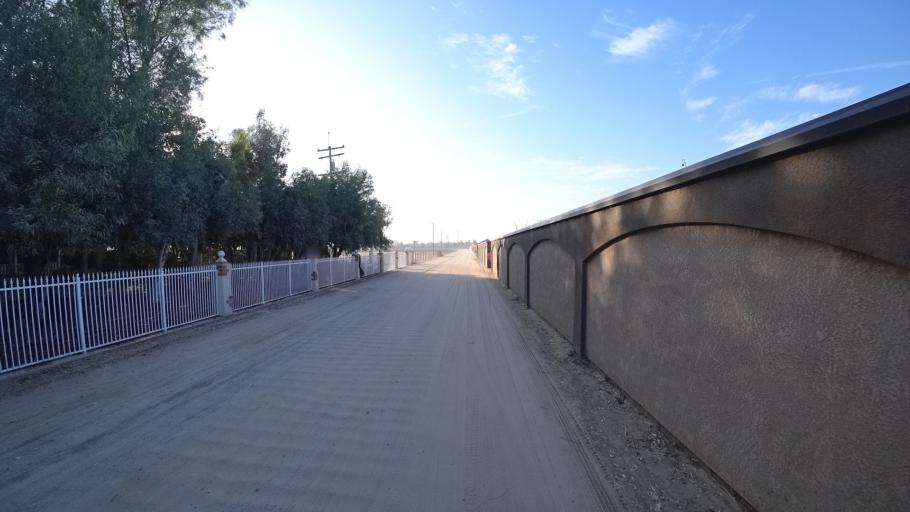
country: US
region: California
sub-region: Kern County
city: Greenacres
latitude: 35.4292
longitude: -119.1234
